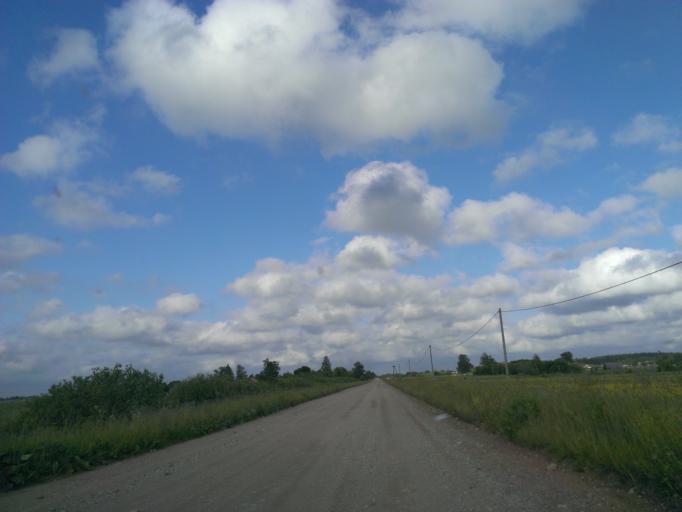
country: LV
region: Aizpute
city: Aizpute
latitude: 56.7517
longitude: 21.4234
